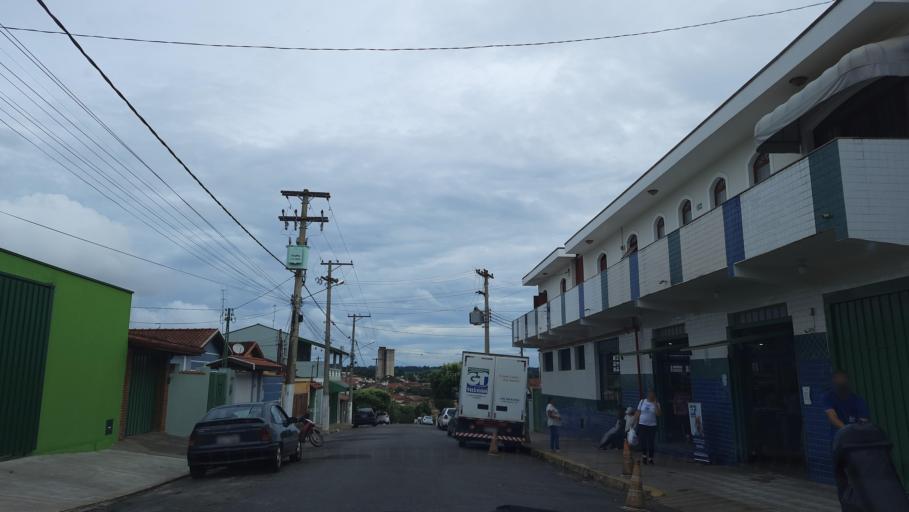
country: BR
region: Sao Paulo
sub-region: Casa Branca
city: Casa Branca
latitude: -21.7652
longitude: -47.0918
